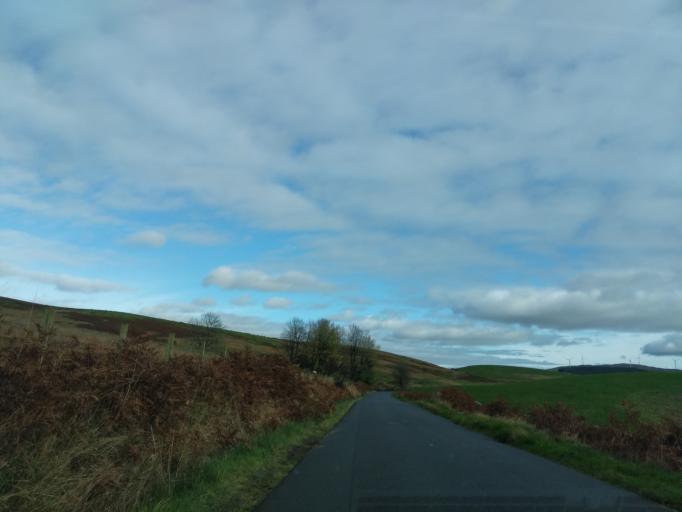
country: GB
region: Scotland
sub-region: Dumfries and Galloway
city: Castle Douglas
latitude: 55.1202
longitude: -4.0854
